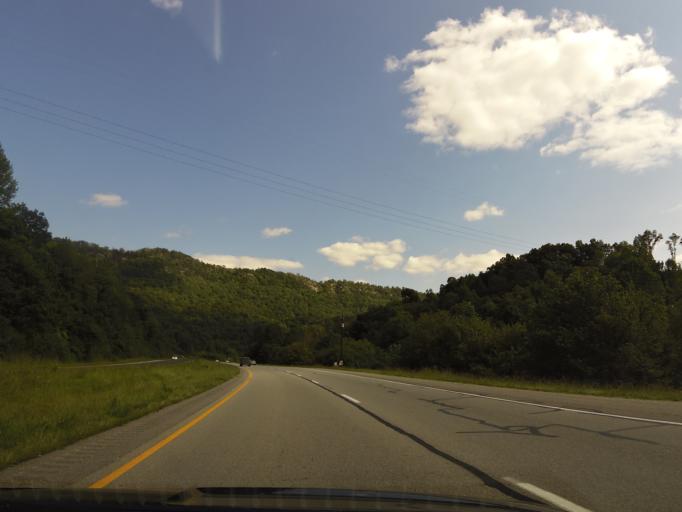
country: US
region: Kentucky
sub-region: Bell County
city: Pineville
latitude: 36.6974
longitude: -83.6906
